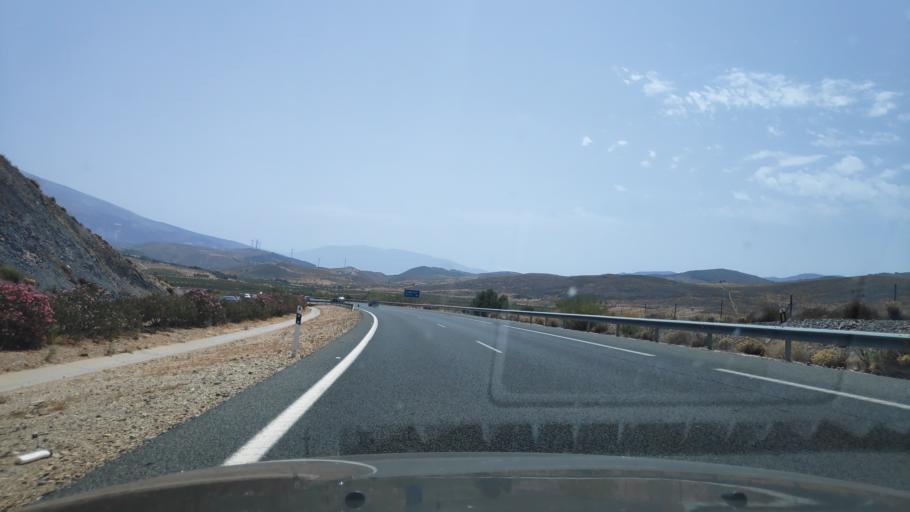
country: ES
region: Andalusia
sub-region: Provincia de Granada
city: Padul
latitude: 36.9932
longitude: -3.6273
